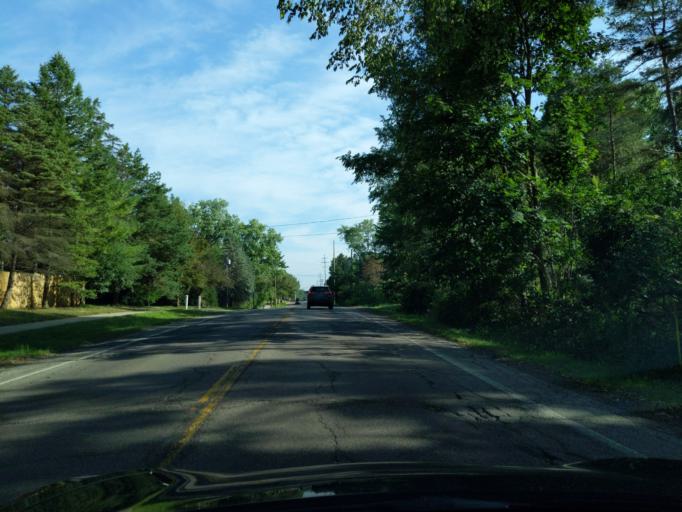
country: US
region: Michigan
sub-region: Ingham County
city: Okemos
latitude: 42.7295
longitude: -84.4276
